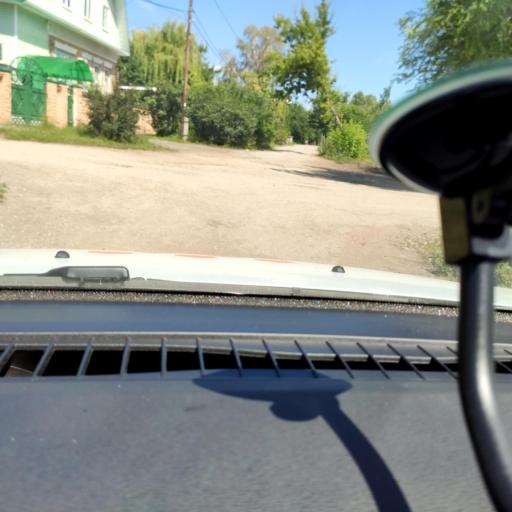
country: RU
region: Samara
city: Petra-Dubrava
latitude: 53.2509
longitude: 50.3334
